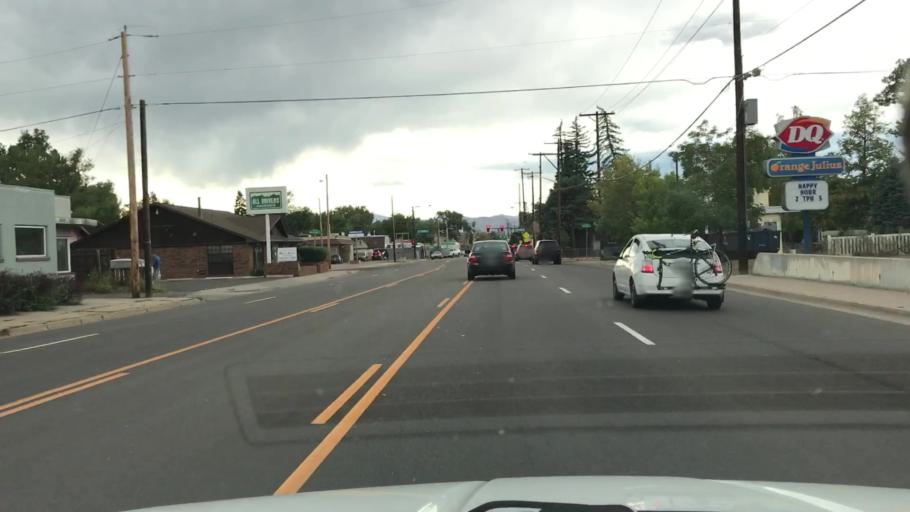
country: US
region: Colorado
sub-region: Jefferson County
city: Edgewater
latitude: 39.7695
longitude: -105.0371
